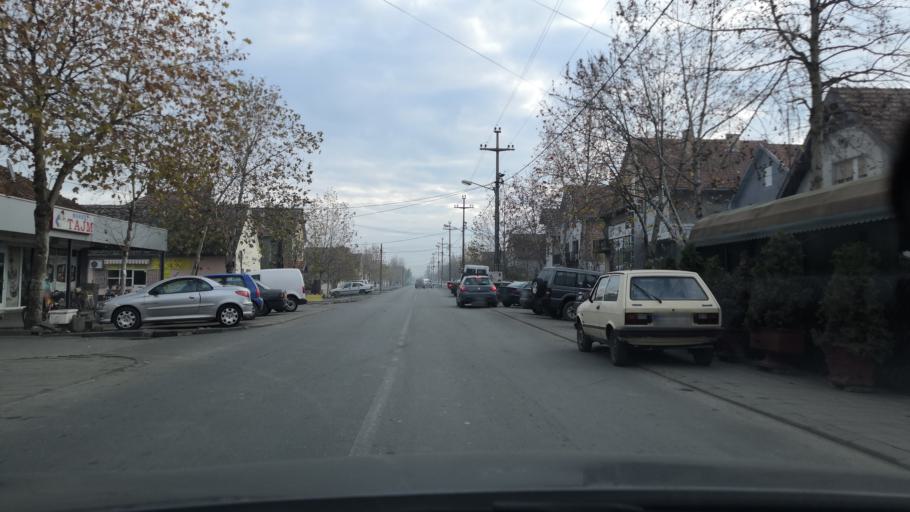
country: RS
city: Ugrinovci
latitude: 44.8754
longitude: 20.1879
